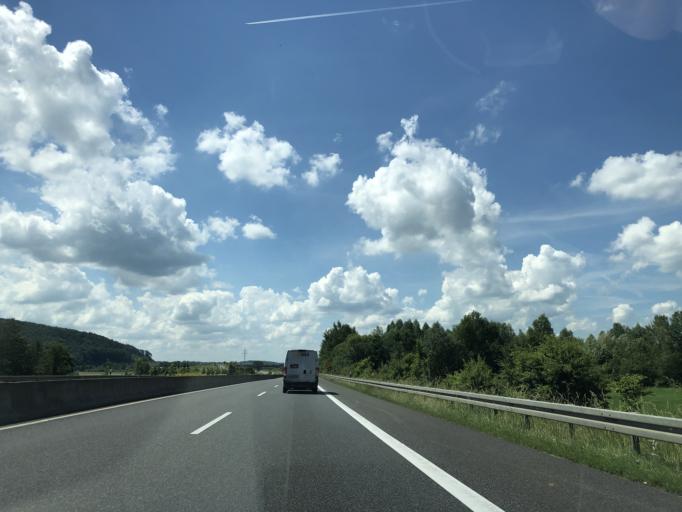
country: DE
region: Hesse
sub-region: Regierungsbezirk Giessen
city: Marburg an der Lahn
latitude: 50.7582
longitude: 8.7443
